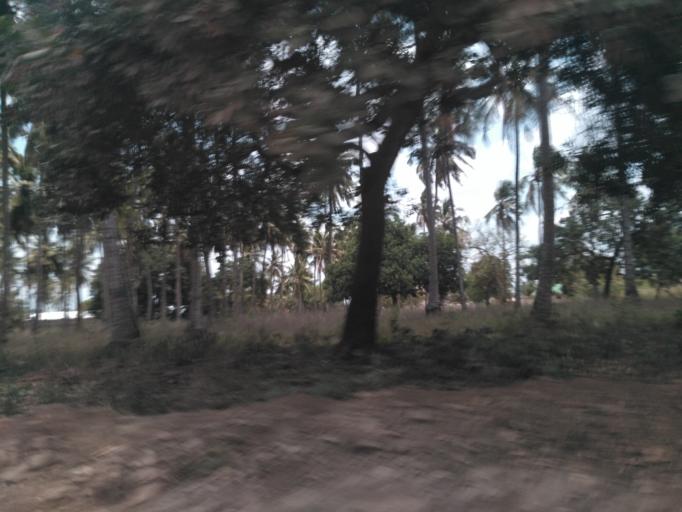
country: TZ
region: Dar es Salaam
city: Dar es Salaam
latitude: -6.8418
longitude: 39.3432
